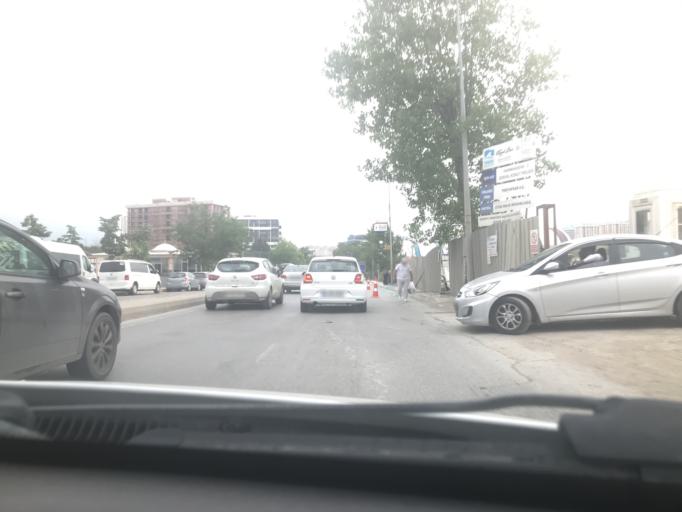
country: TR
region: Istanbul
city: Sultanbeyli
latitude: 40.9293
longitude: 29.3241
